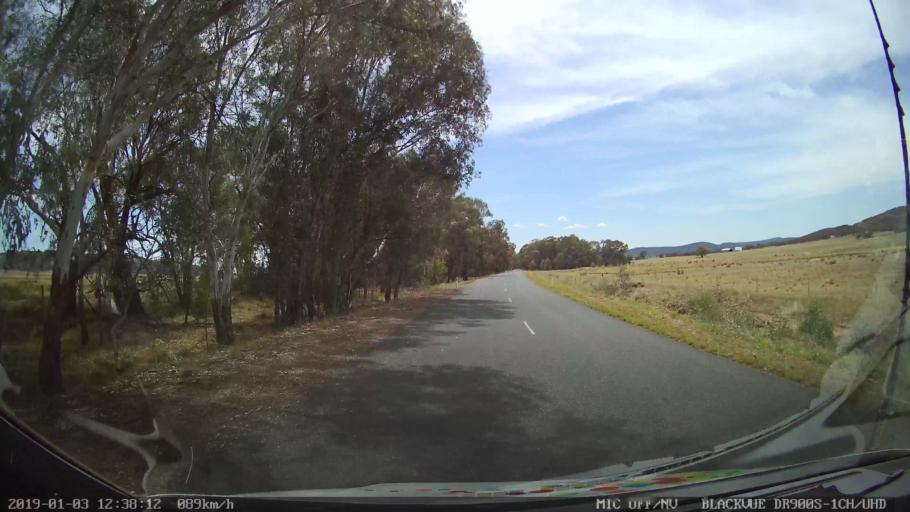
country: AU
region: New South Wales
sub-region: Weddin
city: Grenfell
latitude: -33.8355
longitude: 148.1925
